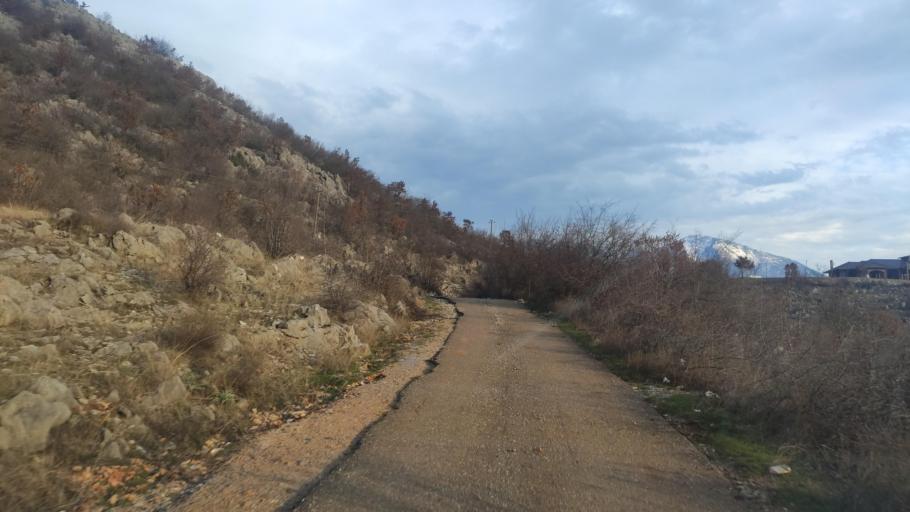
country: AL
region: Shkoder
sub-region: Rrethi i Malesia e Madhe
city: Gruemire
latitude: 42.2386
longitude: 19.5366
